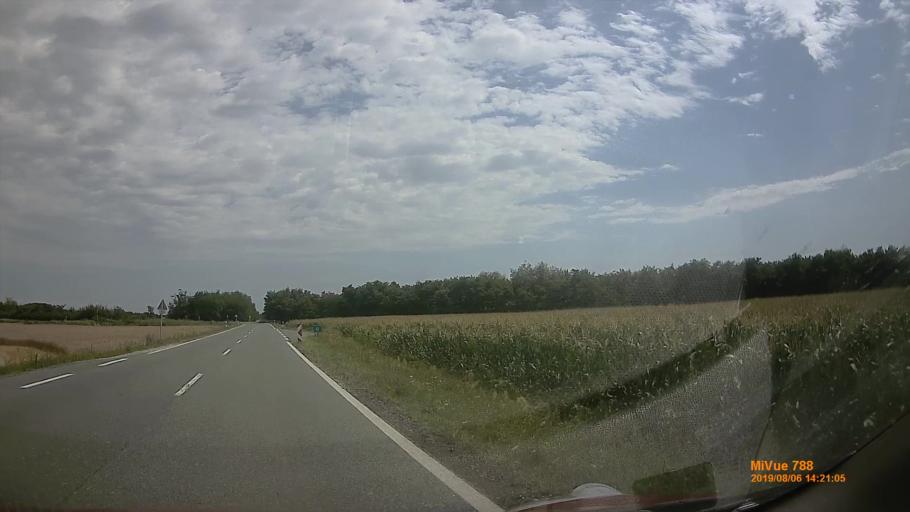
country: HU
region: Vas
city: Vep
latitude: 47.1719
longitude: 16.7689
